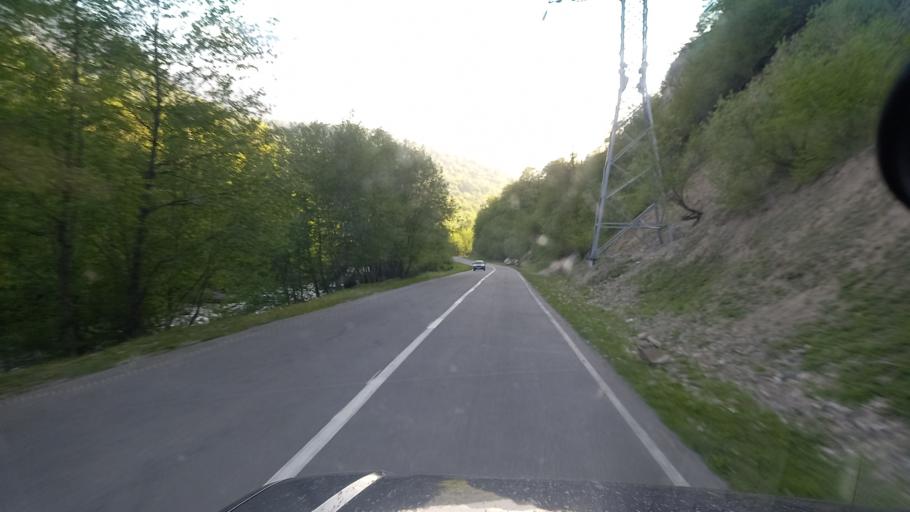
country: RU
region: Ingushetiya
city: Galashki
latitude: 42.9097
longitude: 44.9886
